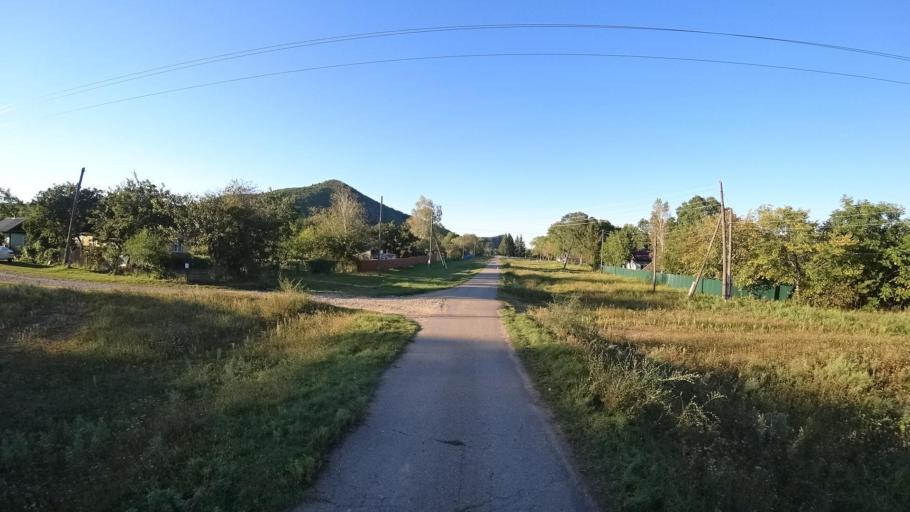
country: RU
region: Primorskiy
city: Kirovskiy
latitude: 44.8291
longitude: 133.5751
